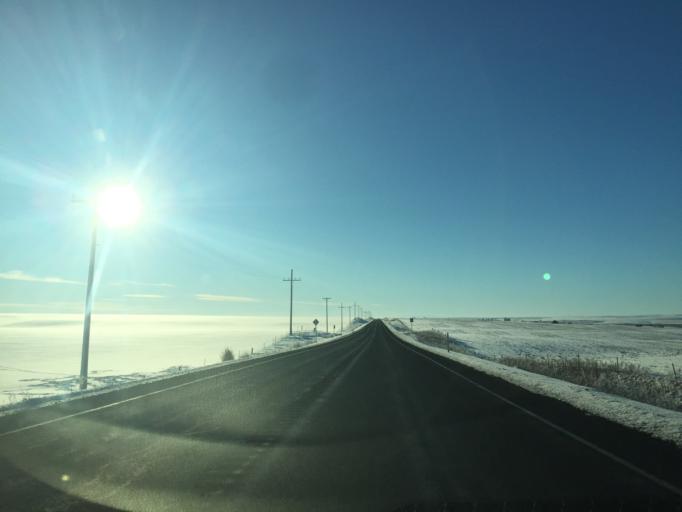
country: US
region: Washington
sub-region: Okanogan County
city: Coulee Dam
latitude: 47.7275
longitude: -118.8772
